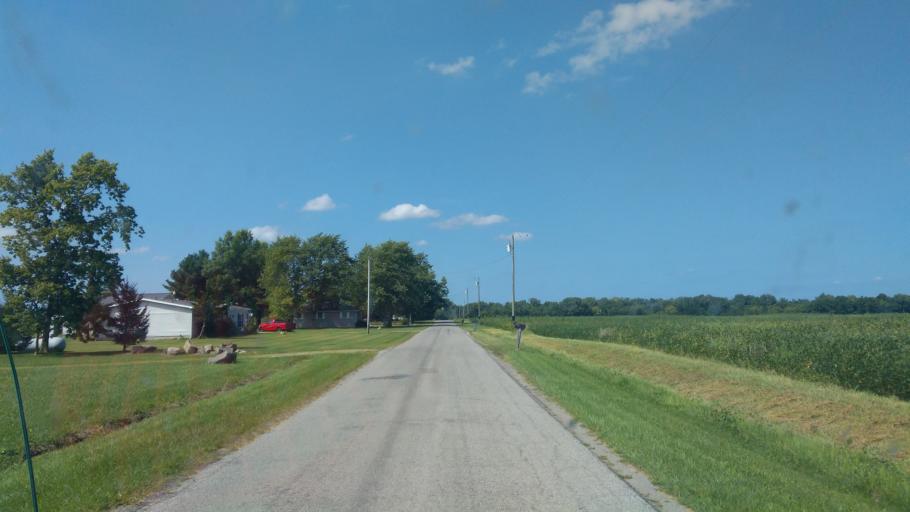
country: US
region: Ohio
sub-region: Union County
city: Richwood
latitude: 40.4690
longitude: -83.3898
